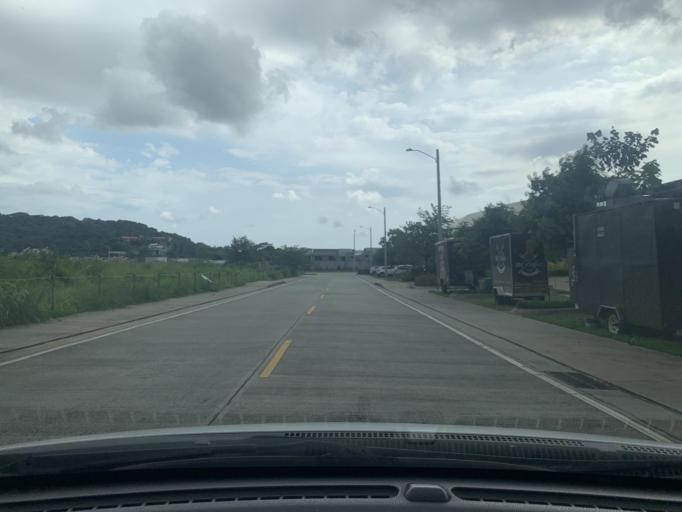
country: PA
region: Panama
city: San Miguelito
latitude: 9.0923
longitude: -79.4683
